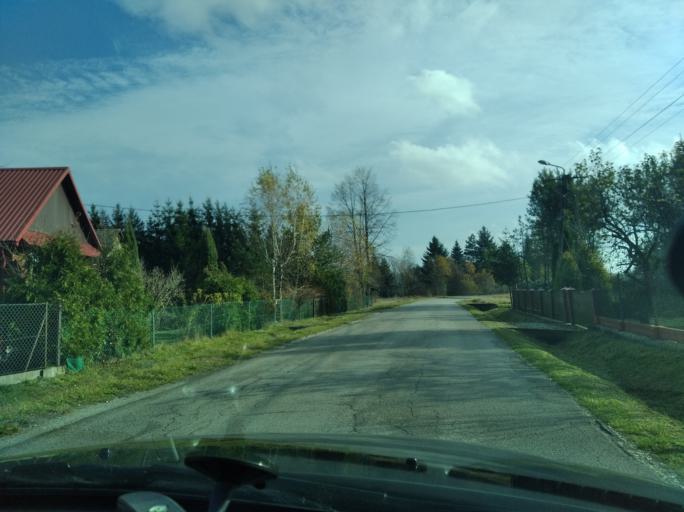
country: PL
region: Subcarpathian Voivodeship
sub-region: Powiat ropczycko-sedziszowski
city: Sedziszow Malopolski
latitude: 50.1188
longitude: 21.7283
